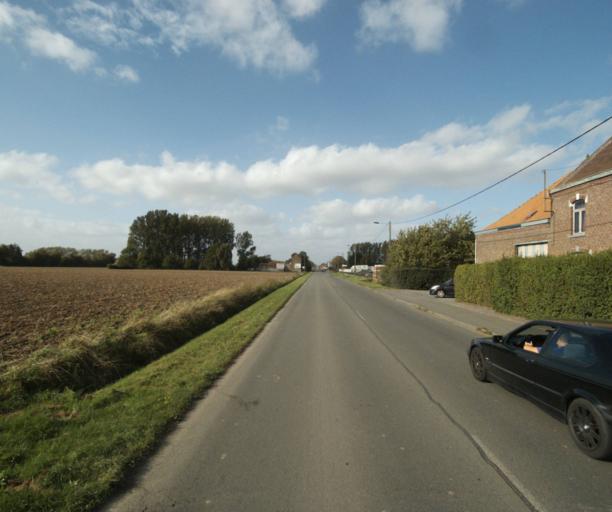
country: FR
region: Nord-Pas-de-Calais
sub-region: Departement du Pas-de-Calais
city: Violaines
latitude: 50.5444
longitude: 2.7980
